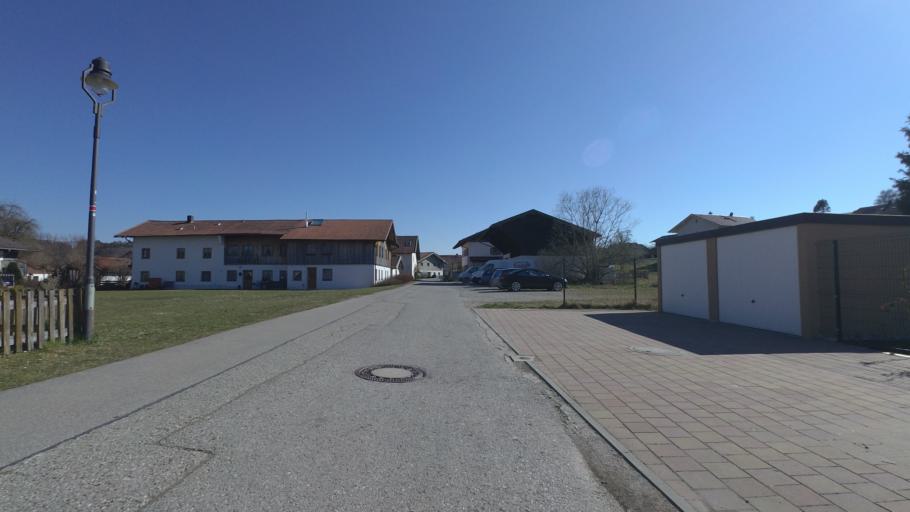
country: DE
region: Bavaria
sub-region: Upper Bavaria
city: Seeon-Seebruck
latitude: 47.9582
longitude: 12.4988
